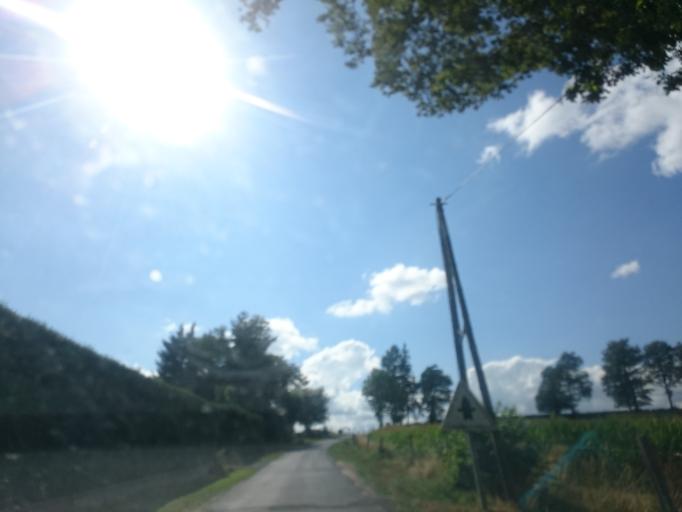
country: FR
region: Auvergne
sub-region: Departement du Cantal
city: Saint-Mamet-la-Salvetat
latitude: 44.8784
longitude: 2.2554
